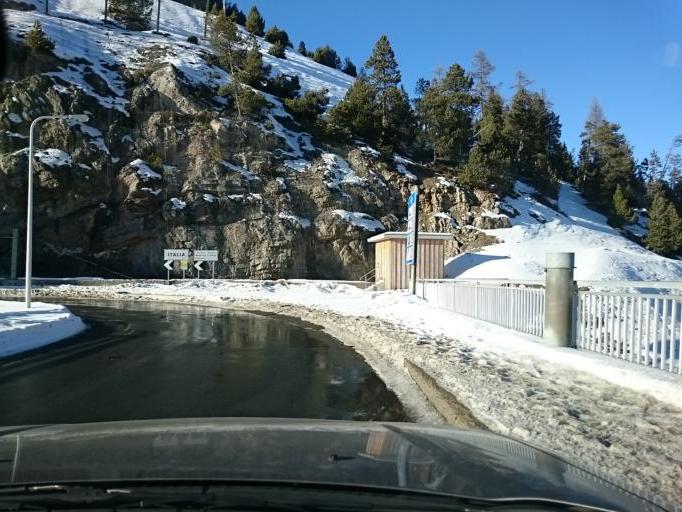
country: IT
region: Lombardy
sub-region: Provincia di Sondrio
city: Livigno
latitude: 46.6245
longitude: 10.1909
